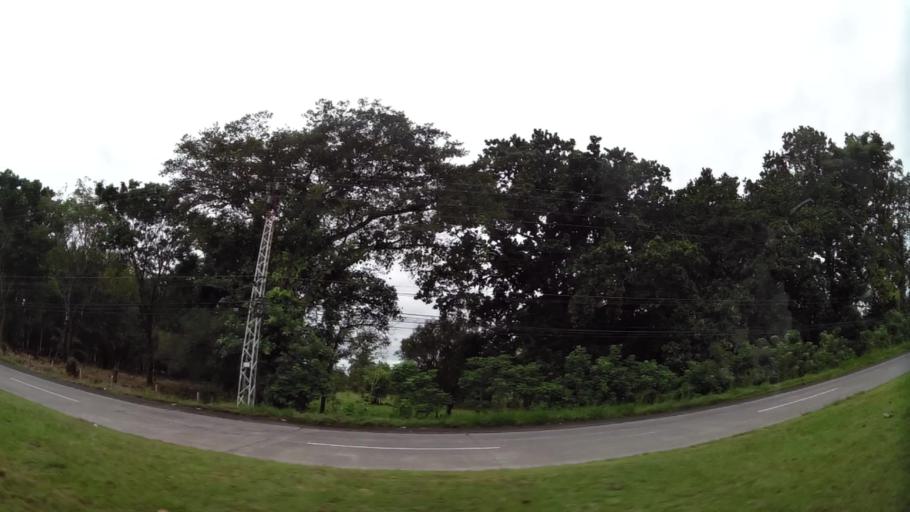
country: PA
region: Chiriqui
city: Boqueron
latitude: 8.4854
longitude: -82.5668
